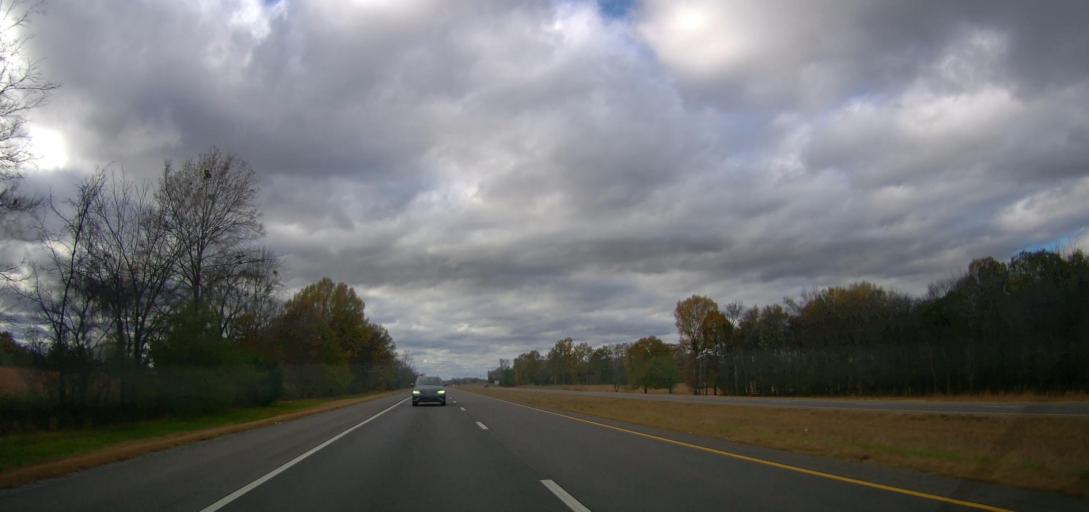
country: US
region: Alabama
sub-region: Lawrence County
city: Moulton
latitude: 34.4591
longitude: -87.2410
